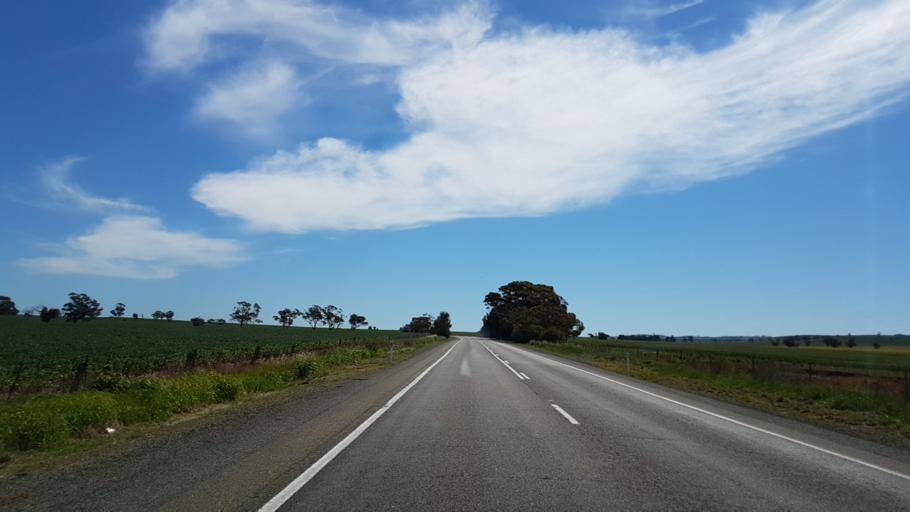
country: AU
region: South Australia
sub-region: Light
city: Freeling
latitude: -34.3315
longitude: 138.7873
